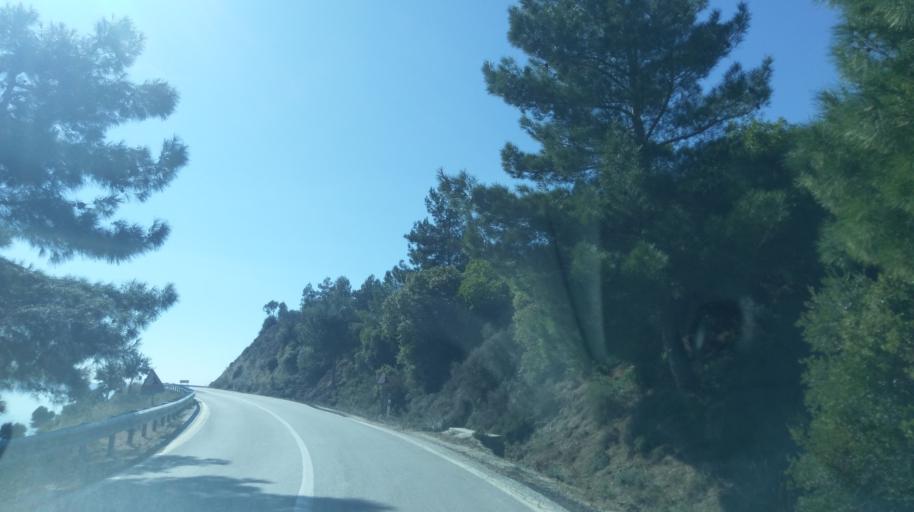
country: TR
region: Canakkale
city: Eceabat
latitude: 40.1077
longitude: 26.3284
